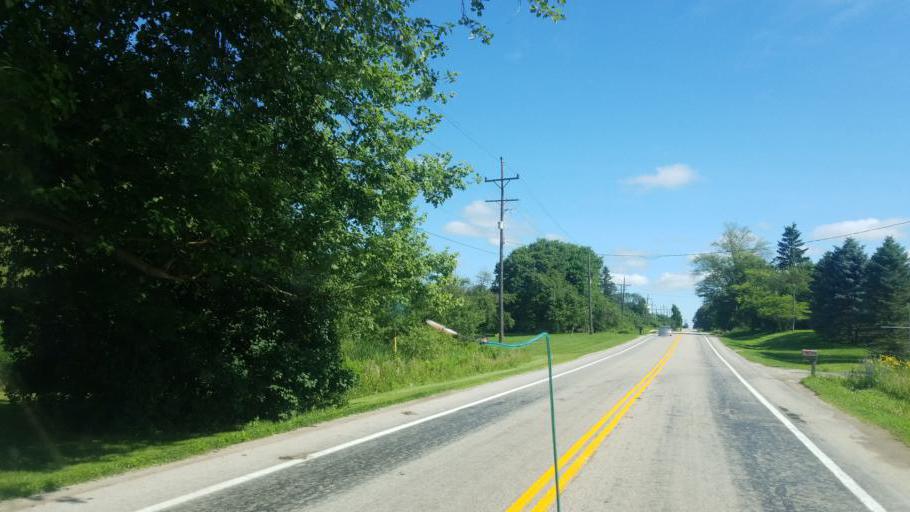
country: US
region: Ohio
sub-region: Ashtabula County
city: Conneaut
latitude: 41.7948
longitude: -80.5722
